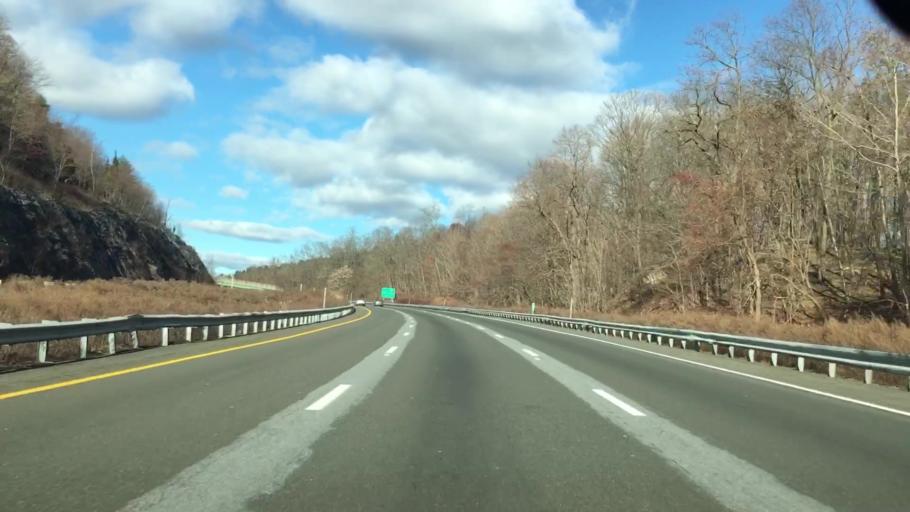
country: US
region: New York
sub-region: Westchester County
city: Bedford
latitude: 41.1767
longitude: -73.6847
